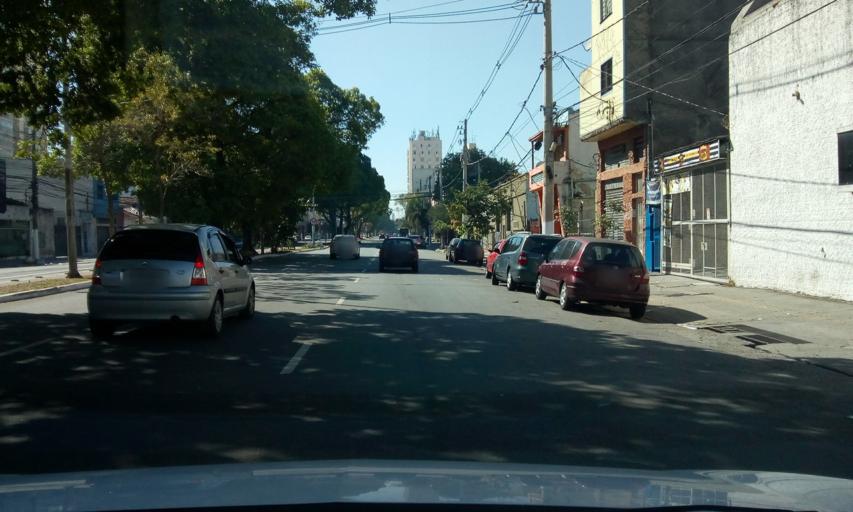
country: BR
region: Sao Paulo
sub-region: Sao Paulo
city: Sao Paulo
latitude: -23.5224
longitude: -46.6487
